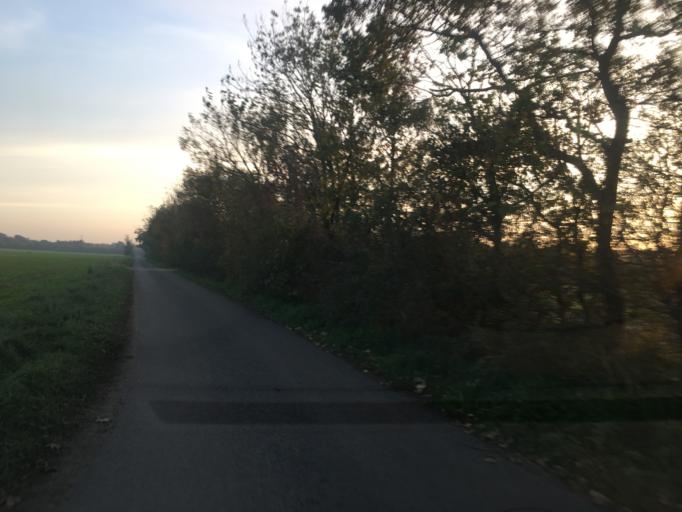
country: DK
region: South Denmark
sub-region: Aabenraa Kommune
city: Tinglev
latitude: 55.0175
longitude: 9.1242
